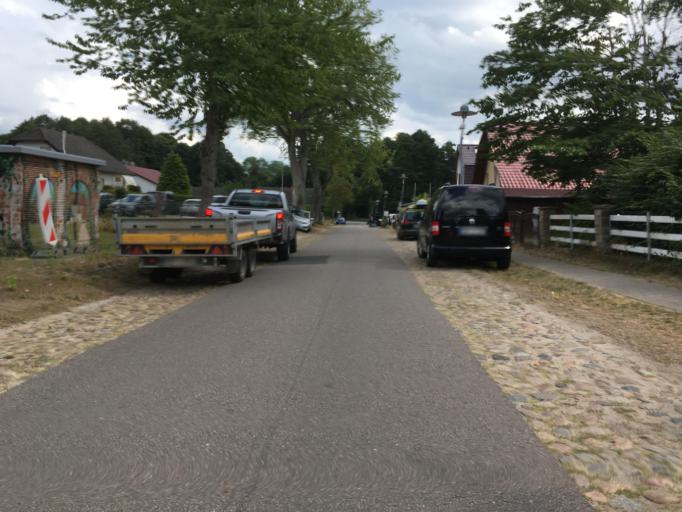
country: DE
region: Brandenburg
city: Lychen
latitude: 53.1735
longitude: 13.2346
